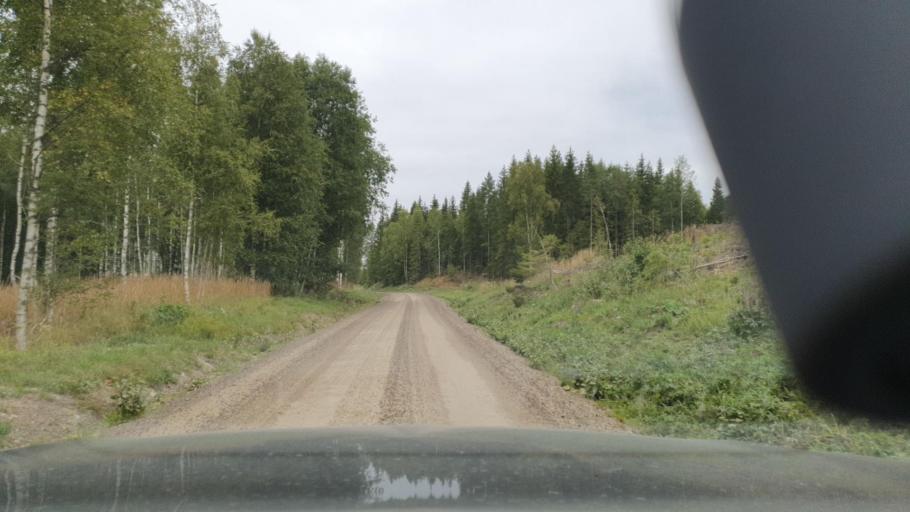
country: SE
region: Vaermland
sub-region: Arvika Kommun
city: Arvika
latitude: 59.9434
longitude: 12.6610
